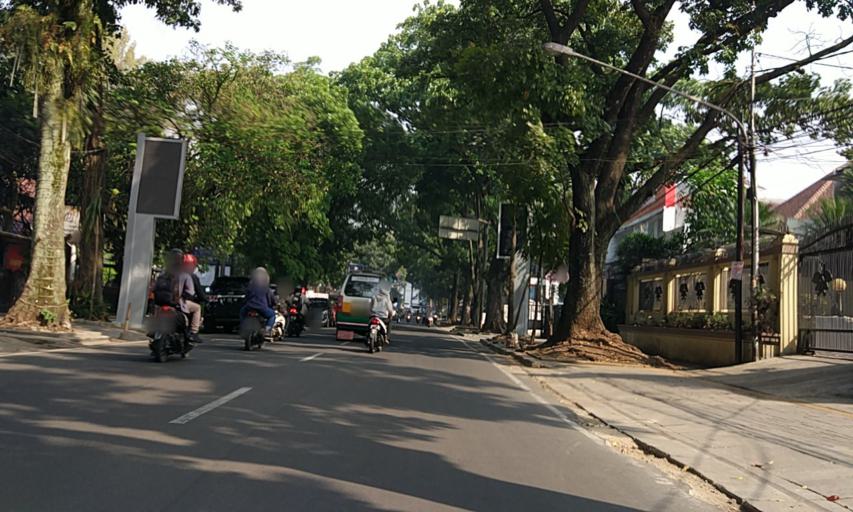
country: ID
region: West Java
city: Bandung
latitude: -6.8999
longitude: 107.6115
